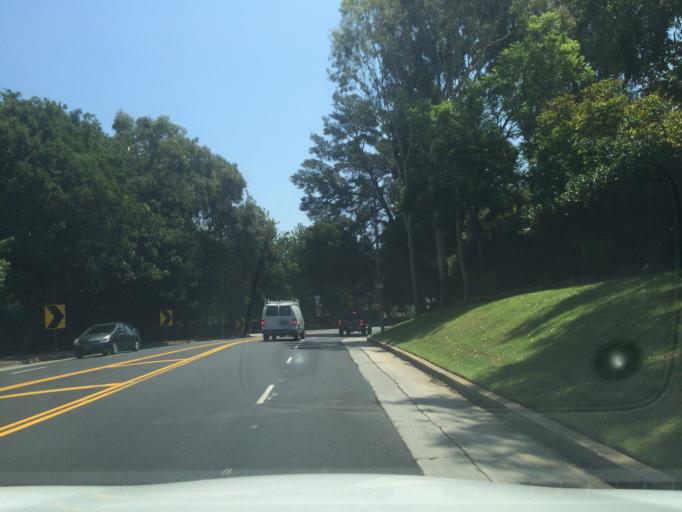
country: US
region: California
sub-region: Los Angeles County
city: Beverly Hills
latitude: 34.0803
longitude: -118.4238
